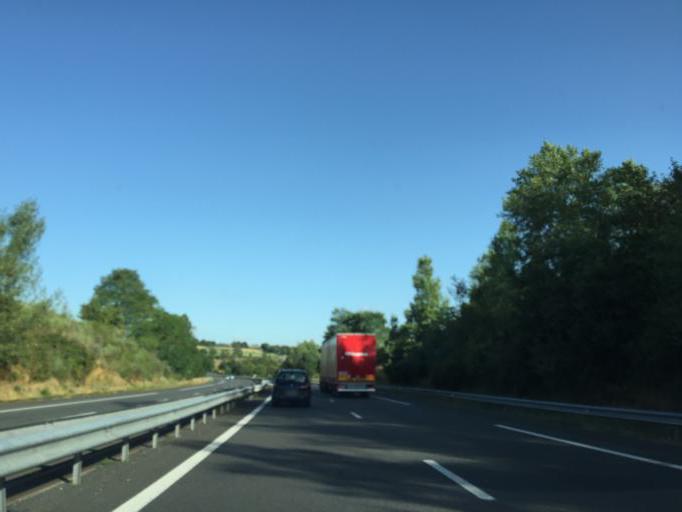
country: FR
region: Auvergne
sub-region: Departement de l'Allier
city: Montmarault
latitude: 46.3336
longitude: 2.8907
